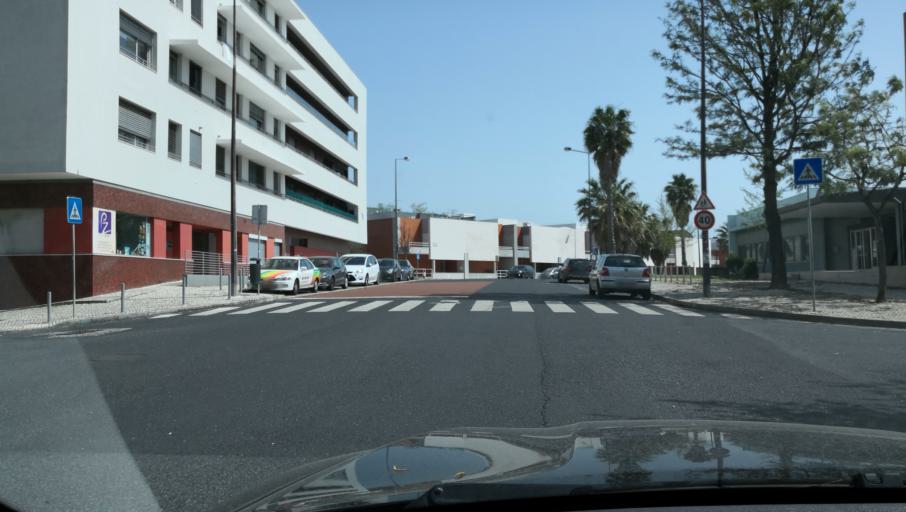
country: PT
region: Lisbon
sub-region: Odivelas
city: Olival do Basto
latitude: 38.7680
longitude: -9.1680
